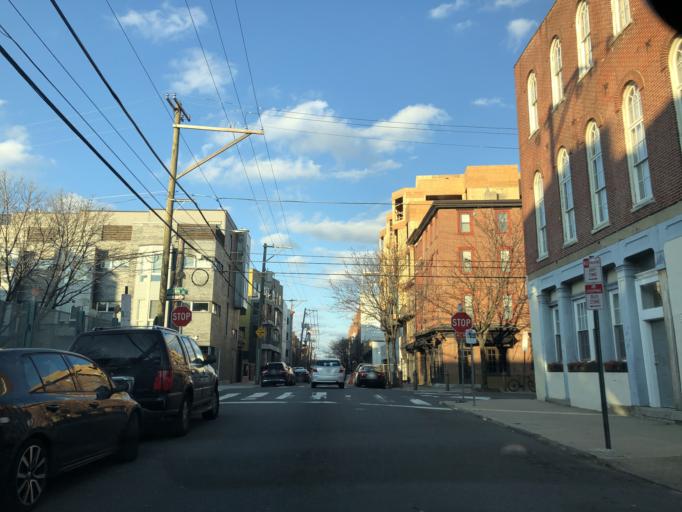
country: US
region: Pennsylvania
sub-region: Philadelphia County
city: Philadelphia
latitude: 39.9631
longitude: -75.1429
